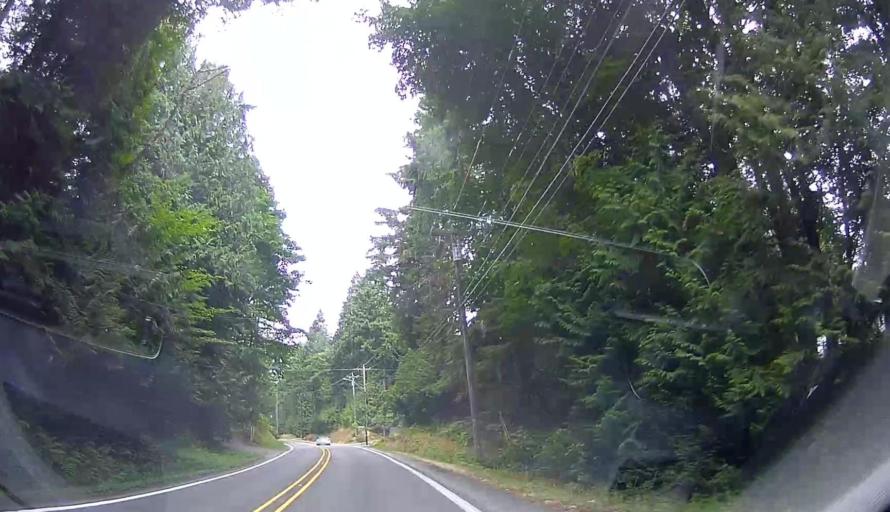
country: US
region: Washington
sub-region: Snohomish County
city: Tulalip
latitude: 48.1090
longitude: -122.3312
